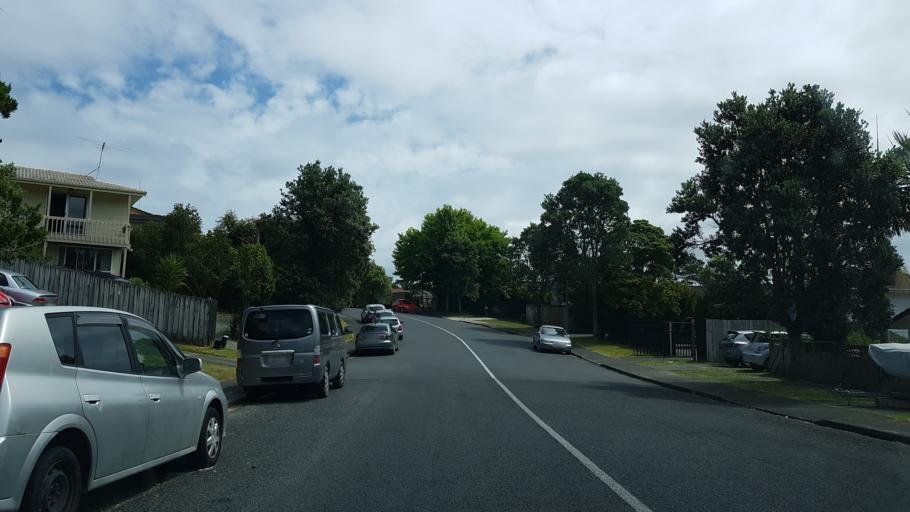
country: NZ
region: Auckland
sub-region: Auckland
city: North Shore
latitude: -36.7711
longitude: 174.7167
